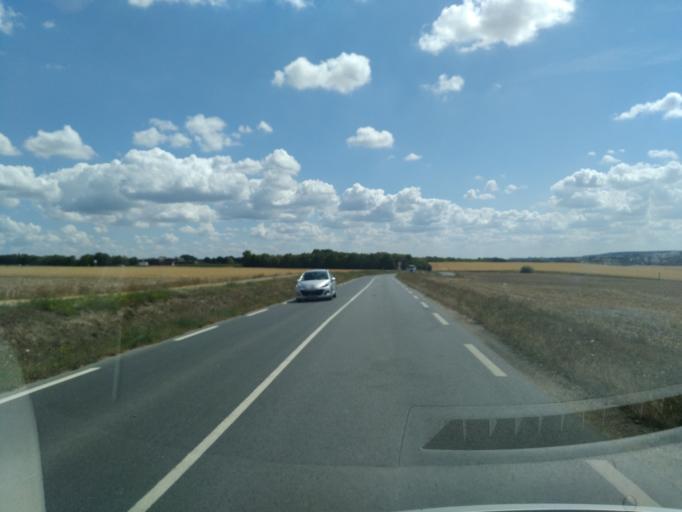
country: FR
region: Ile-de-France
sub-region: Departement des Yvelines
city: Plaisir
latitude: 48.8382
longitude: 1.9391
